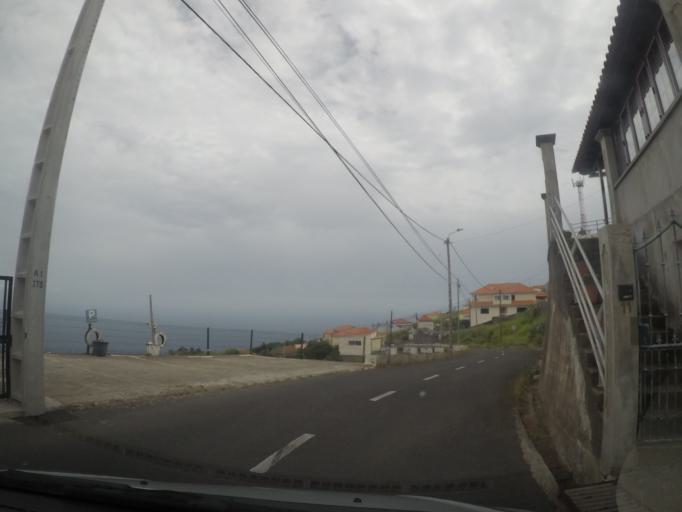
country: PT
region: Madeira
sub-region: Santa Cruz
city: Santa Cruz
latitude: 32.6850
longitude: -16.8104
